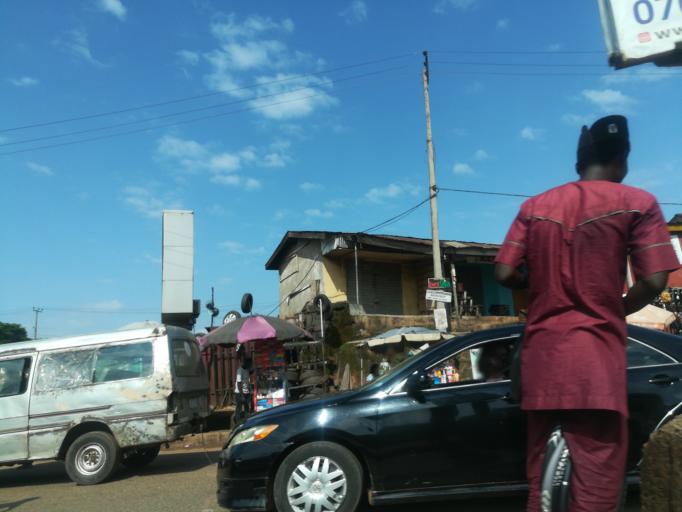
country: NG
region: Oyo
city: Ibadan
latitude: 7.4042
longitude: 3.9443
